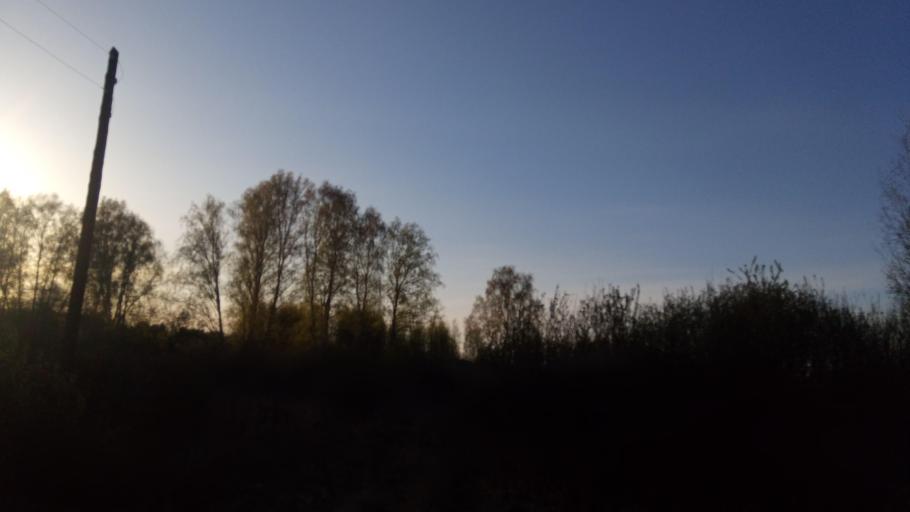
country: RU
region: Chelyabinsk
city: Timiryazevskiy
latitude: 54.9944
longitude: 60.8436
